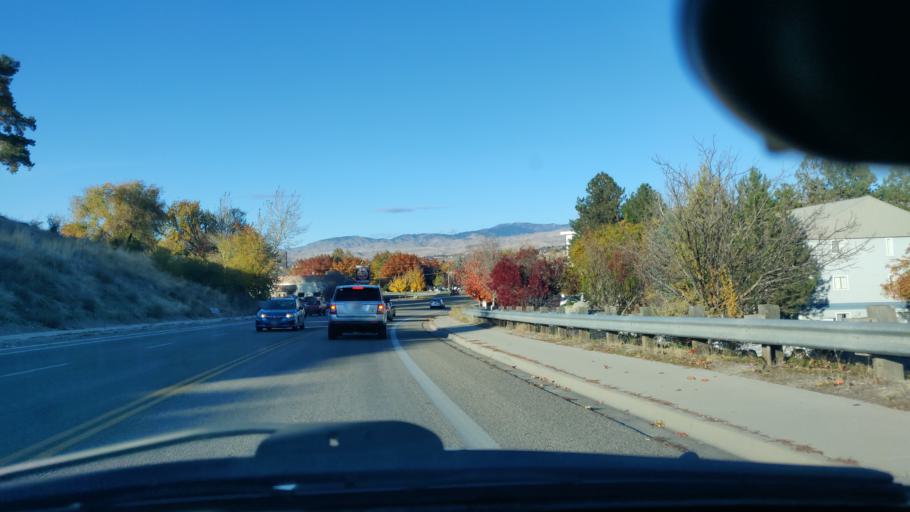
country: US
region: Idaho
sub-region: Ada County
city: Boise
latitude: 43.5962
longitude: -116.2060
